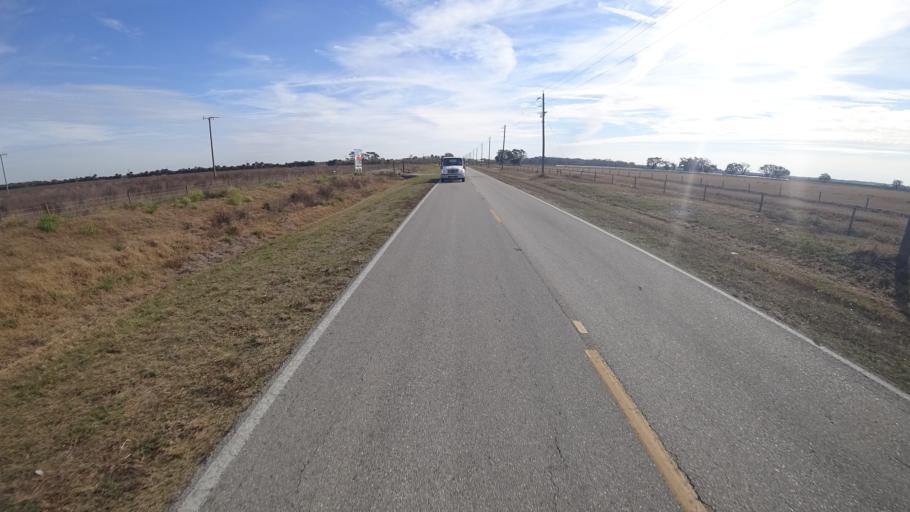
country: US
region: Florida
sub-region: Manatee County
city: Ellenton
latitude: 27.6012
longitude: -82.4853
